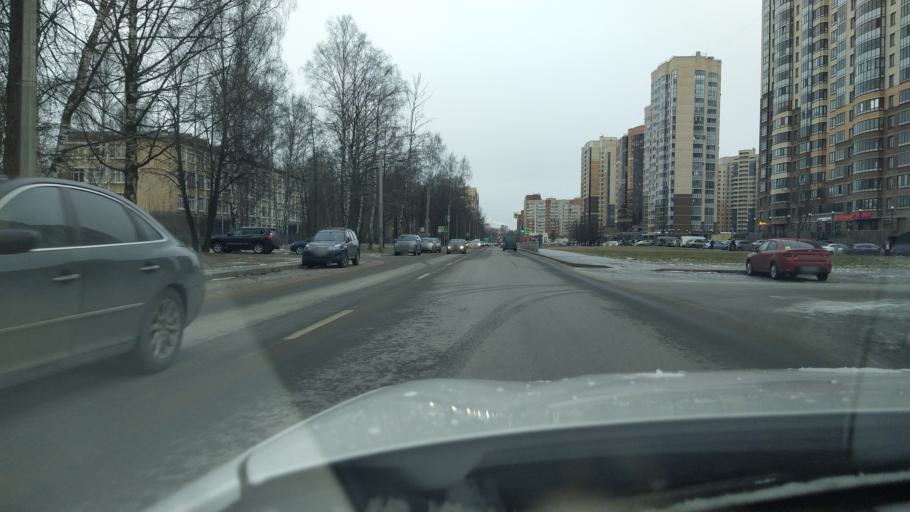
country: RU
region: Leningrad
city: Kalininskiy
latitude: 60.0026
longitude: 30.3975
